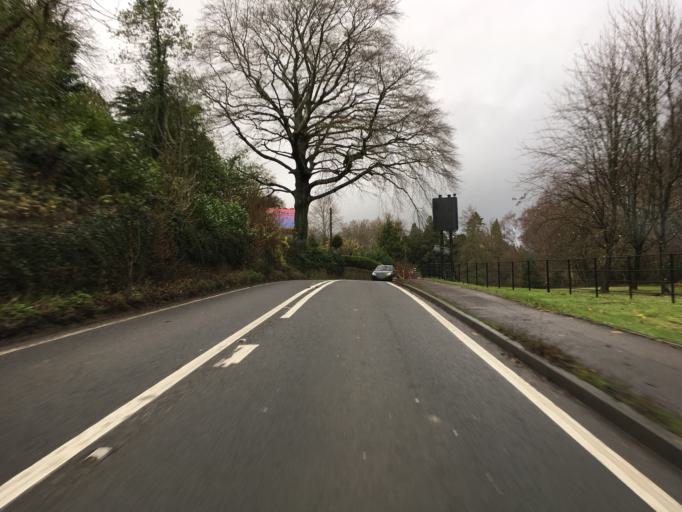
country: GB
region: England
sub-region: Gloucestershire
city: Nailsworth
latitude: 51.7050
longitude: -2.2286
